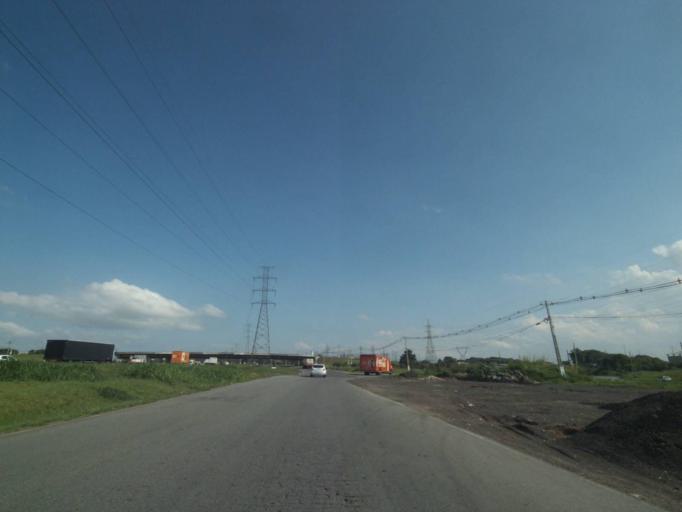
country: BR
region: Parana
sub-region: Araucaria
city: Araucaria
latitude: -25.5208
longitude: -49.3348
